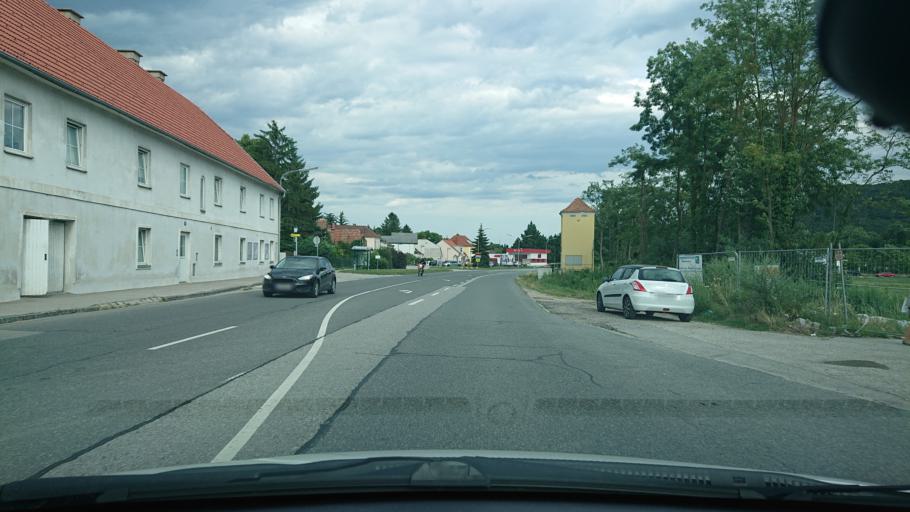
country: AT
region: Lower Austria
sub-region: Politischer Bezirk Baden
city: Berndorf
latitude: 47.9393
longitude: 16.1428
